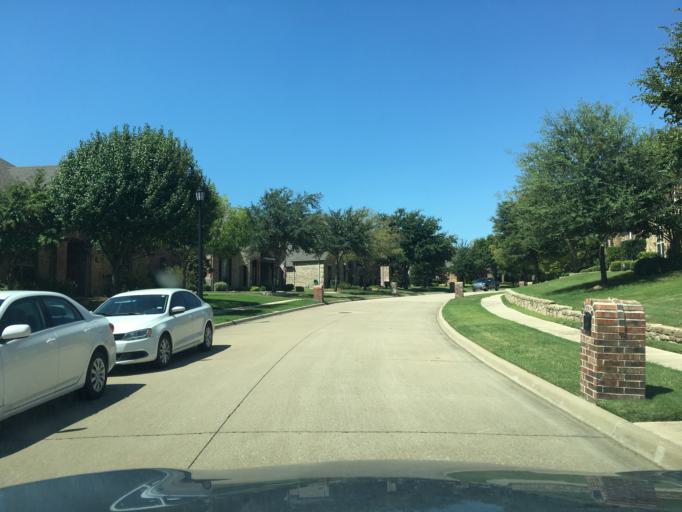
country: US
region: Texas
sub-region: Dallas County
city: Sachse
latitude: 32.9676
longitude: -96.6138
